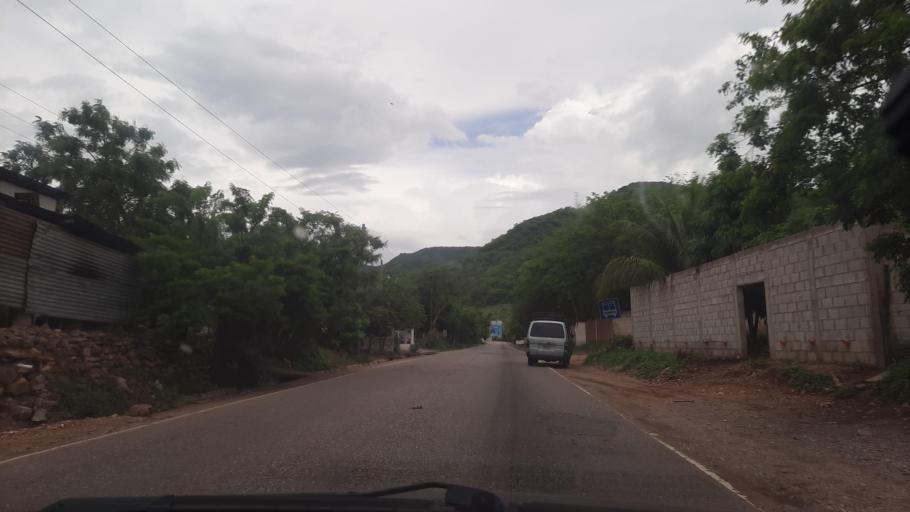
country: GT
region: Zacapa
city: San Jorge
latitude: 14.8975
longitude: -89.5218
